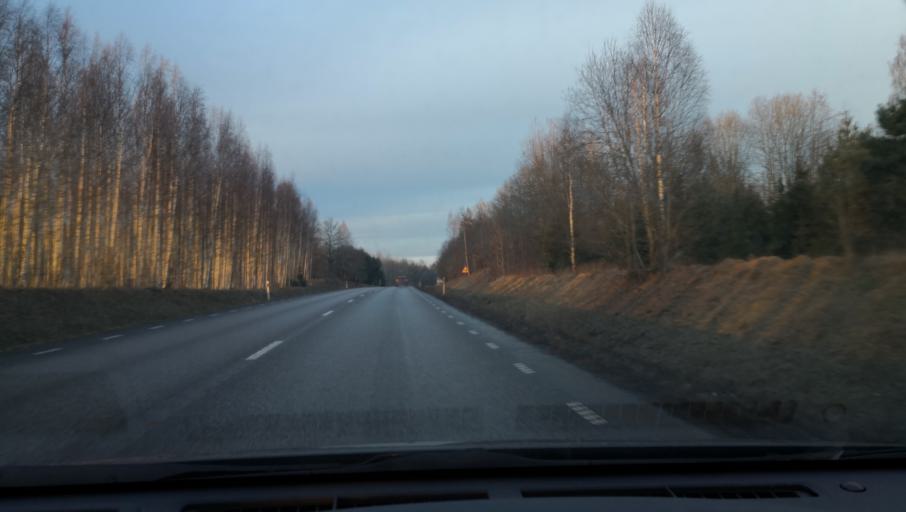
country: SE
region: OErebro
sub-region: Lekebergs Kommun
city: Fjugesta
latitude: 59.1797
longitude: 14.8585
